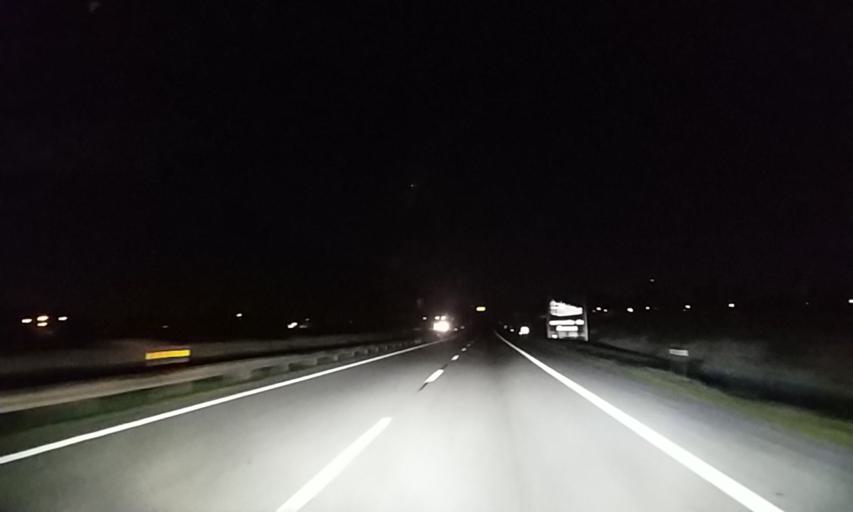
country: PT
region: Aveiro
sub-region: Estarreja
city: Beduido
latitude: 40.7628
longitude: -8.5407
